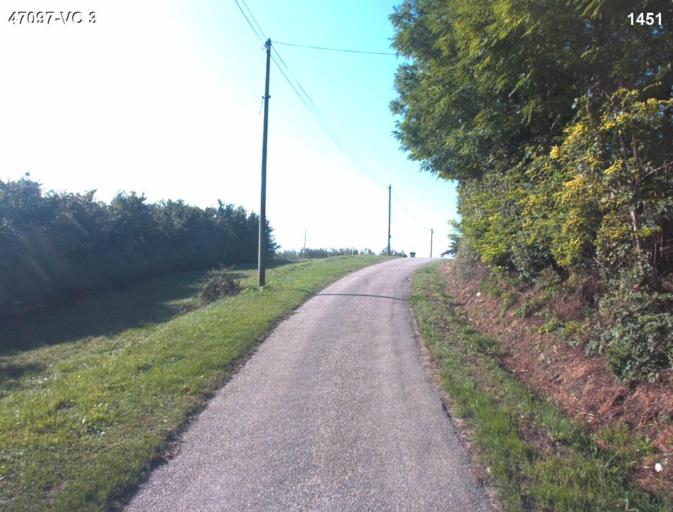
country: FR
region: Aquitaine
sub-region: Departement du Lot-et-Garonne
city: Vianne
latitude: 44.1936
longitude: 0.3520
